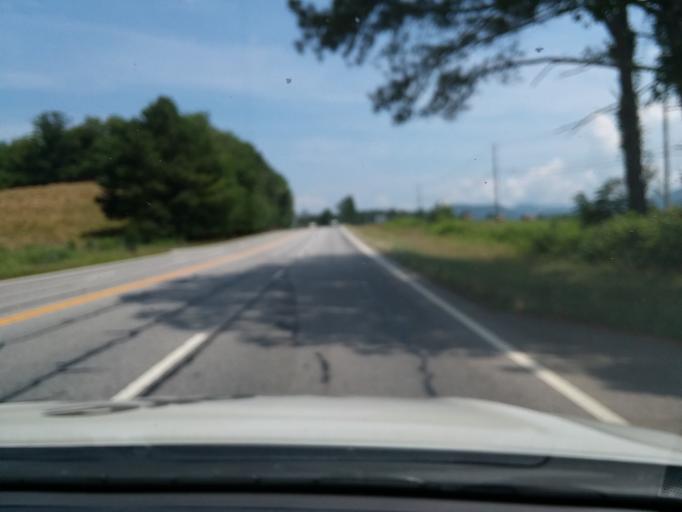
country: US
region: Georgia
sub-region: Rabun County
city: Mountain City
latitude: 34.9526
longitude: -83.3864
